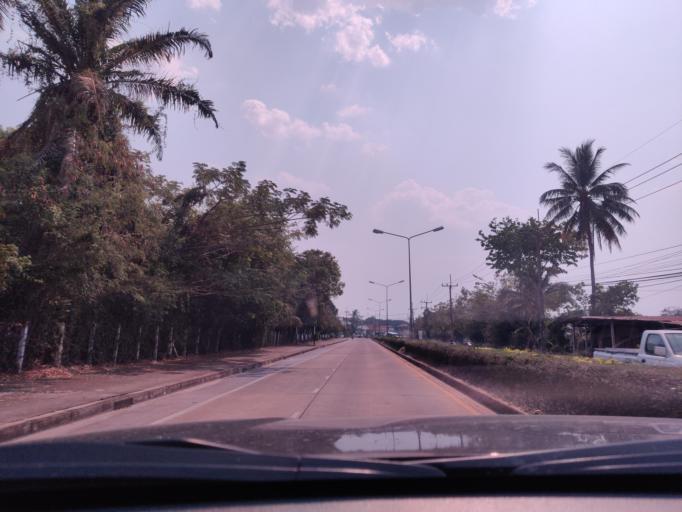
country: TH
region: Sisaket
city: Si Sa Ket
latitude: 15.1024
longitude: 104.3149
